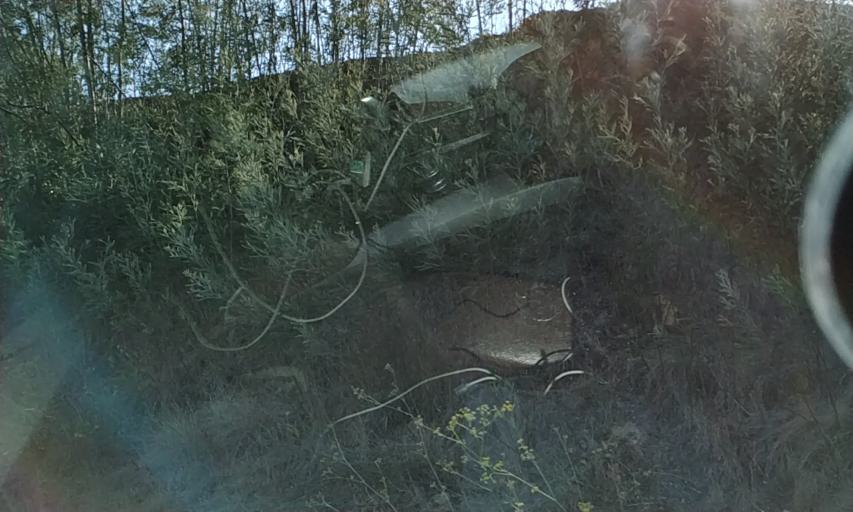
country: PT
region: Evora
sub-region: Vendas Novas
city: Vendas Novas
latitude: 38.7649
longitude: -8.6194
